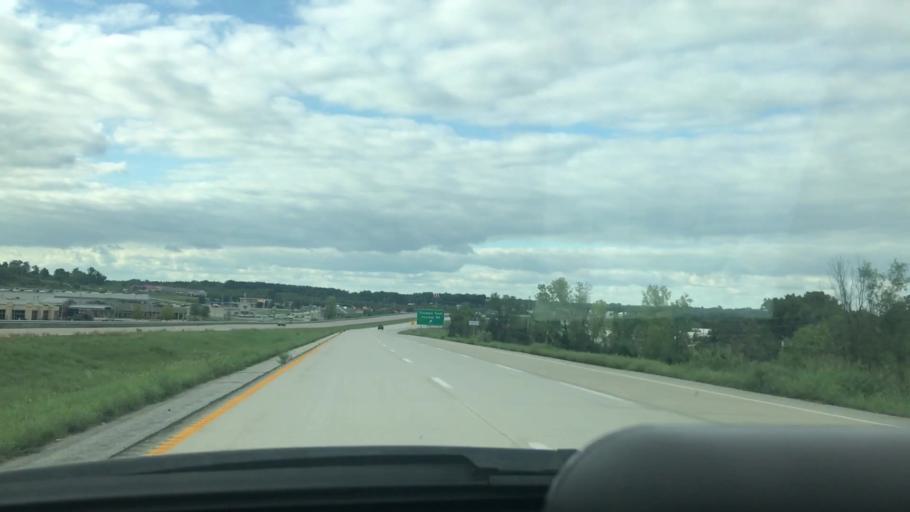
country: US
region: Missouri
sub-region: Benton County
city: Warsaw
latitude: 38.2577
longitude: -93.3665
